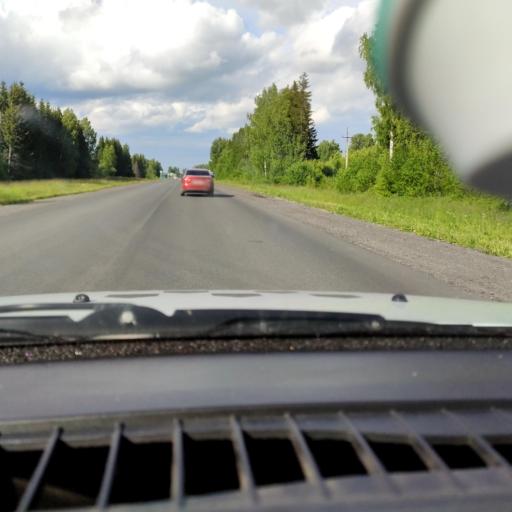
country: RU
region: Perm
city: Orda
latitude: 57.2627
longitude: 57.0136
